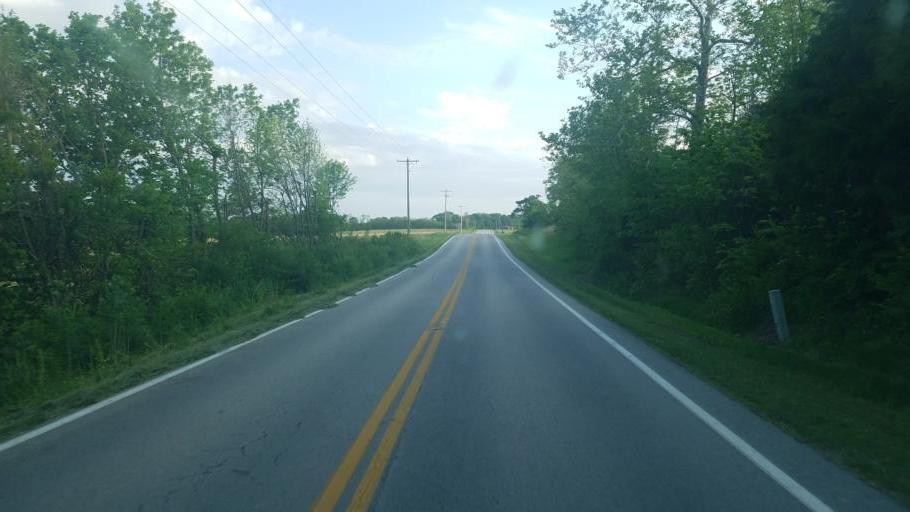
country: US
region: Ohio
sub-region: Highland County
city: Leesburg
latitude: 39.3830
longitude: -83.5944
